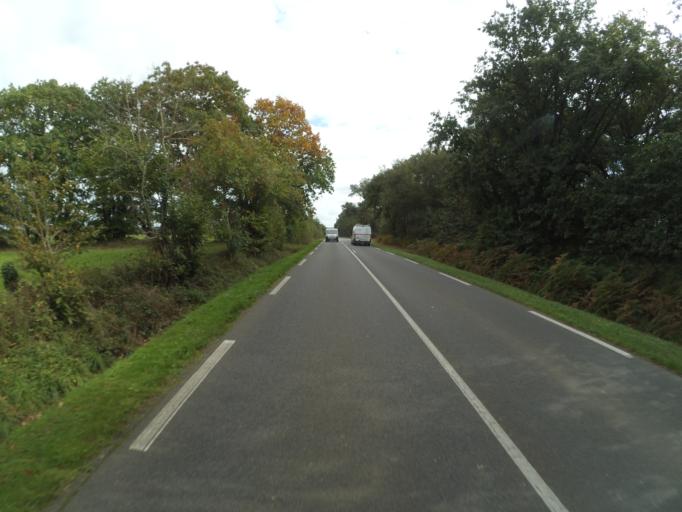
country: FR
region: Pays de la Loire
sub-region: Departement de la Loire-Atlantique
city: Guenrouet
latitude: 47.5727
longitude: -1.9795
